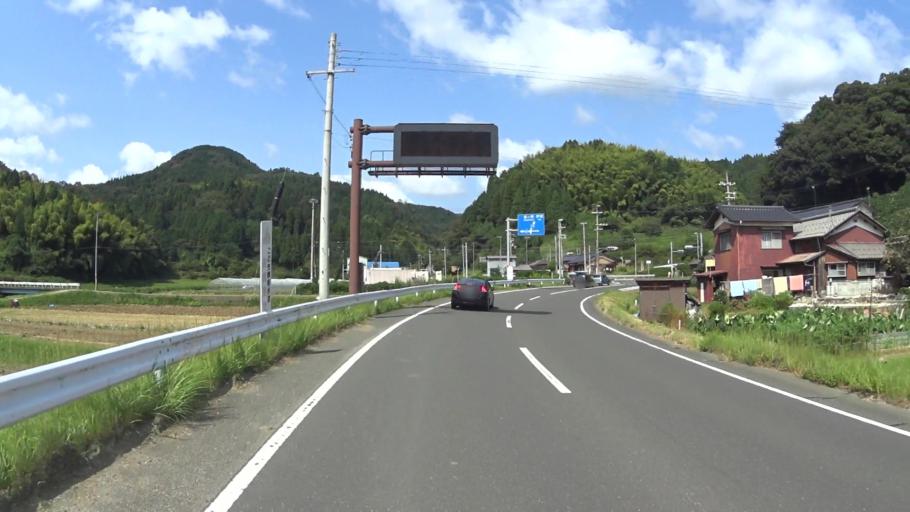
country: JP
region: Kyoto
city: Miyazu
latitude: 35.6578
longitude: 135.2577
